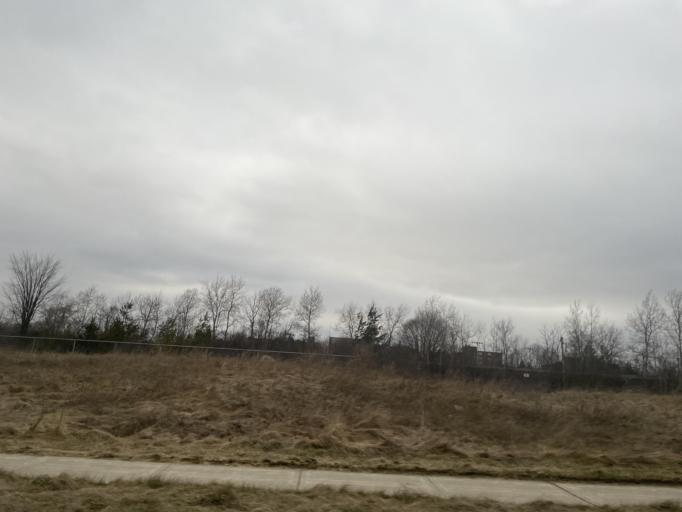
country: CA
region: Ontario
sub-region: Wellington County
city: Guelph
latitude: 43.5303
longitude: -80.2777
